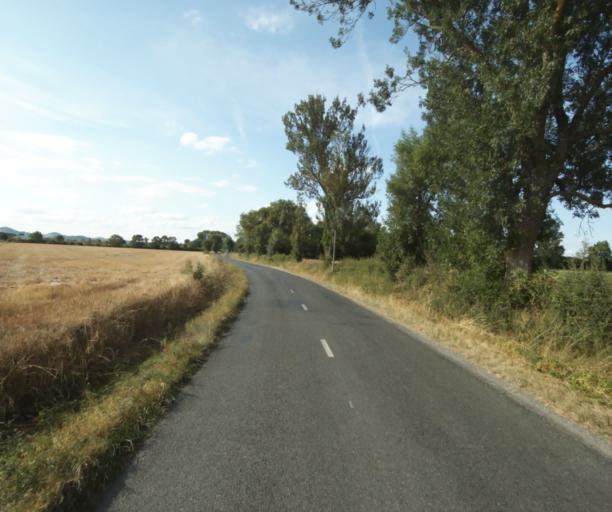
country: FR
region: Midi-Pyrenees
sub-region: Departement de la Haute-Garonne
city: Revel
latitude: 43.4780
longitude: 1.9907
